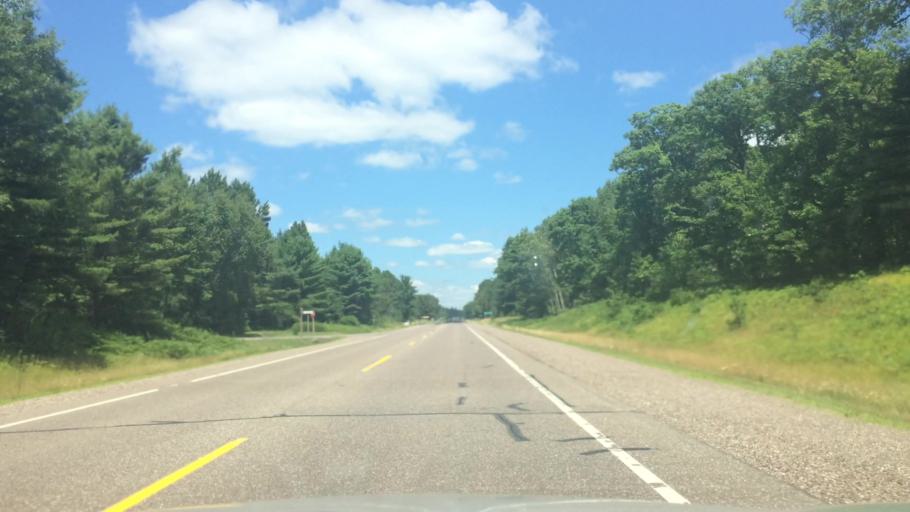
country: US
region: Wisconsin
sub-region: Vilas County
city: Lac du Flambeau
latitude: 45.9699
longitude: -89.6997
